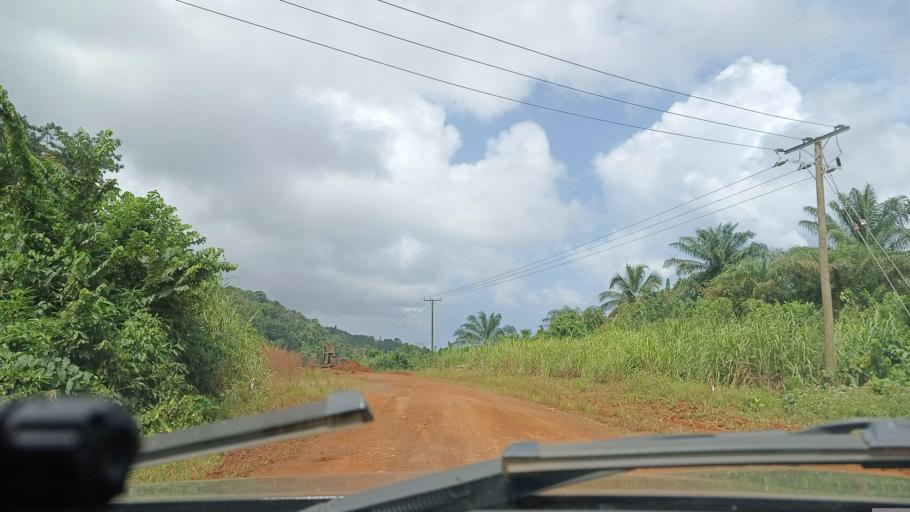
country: LR
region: Grand Cape Mount
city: Robertsport
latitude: 6.7484
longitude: -11.3557
